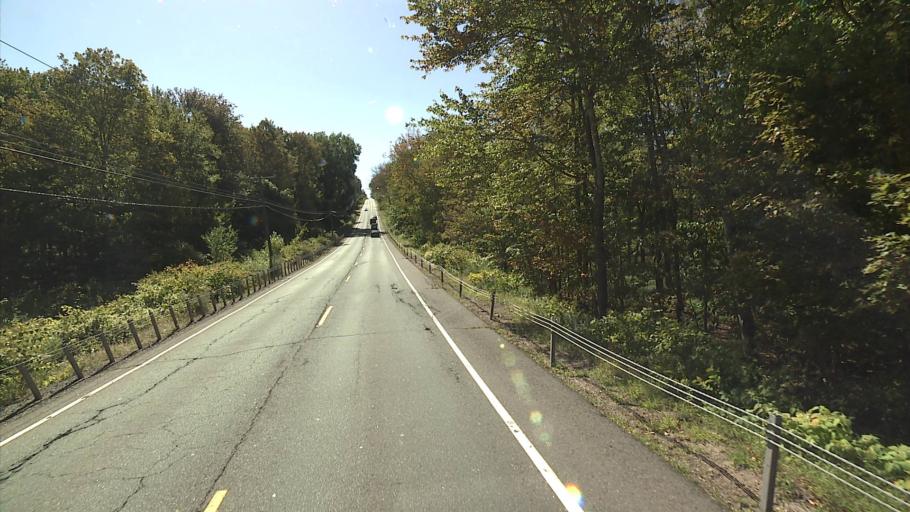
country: US
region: Connecticut
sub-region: New Haven County
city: Prospect
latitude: 41.4810
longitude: -72.9705
